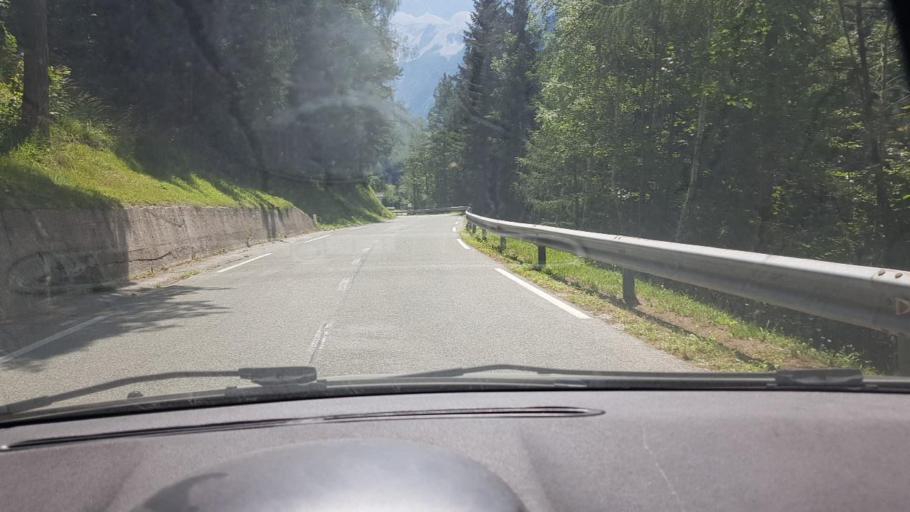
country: SI
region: Jezersko
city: Zgornje Jezersko
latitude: 46.4084
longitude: 14.5264
